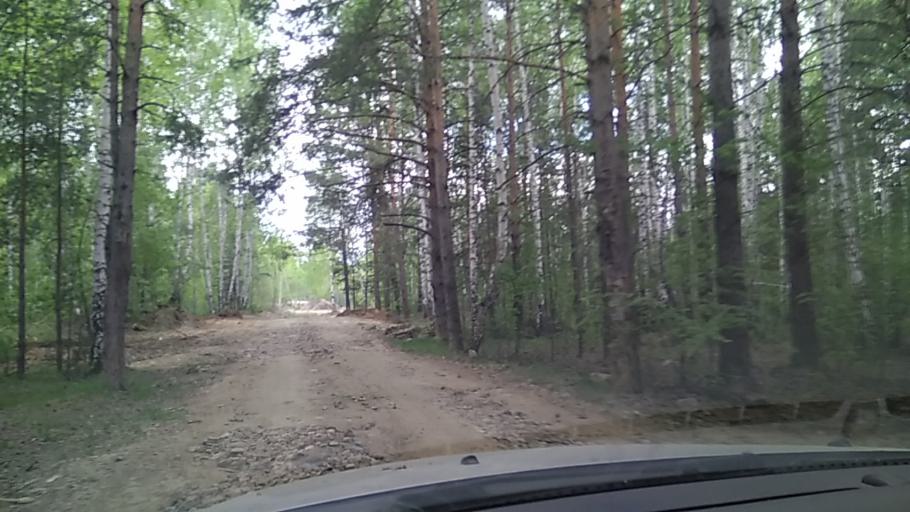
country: RU
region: Sverdlovsk
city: Verkhnyaya Pyshma
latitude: 56.9238
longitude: 60.5986
